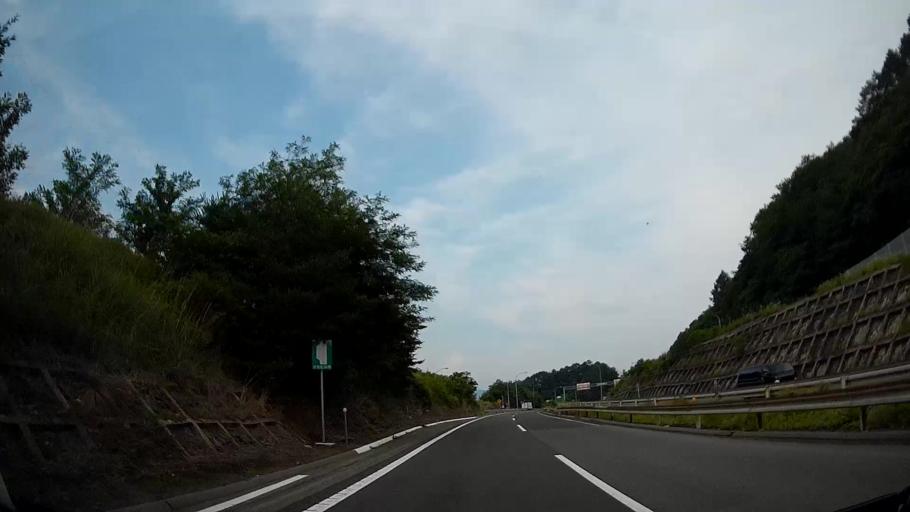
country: JP
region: Nagano
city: Okaya
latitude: 36.0522
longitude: 138.0447
